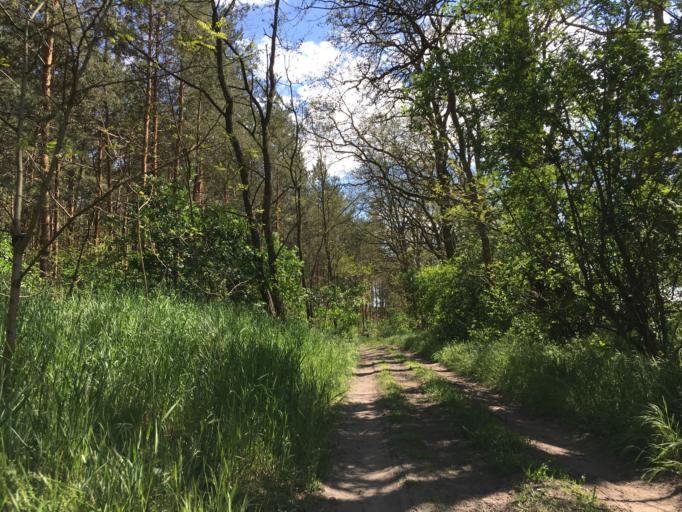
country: DE
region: Brandenburg
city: Rudnitz
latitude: 52.7156
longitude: 13.6573
